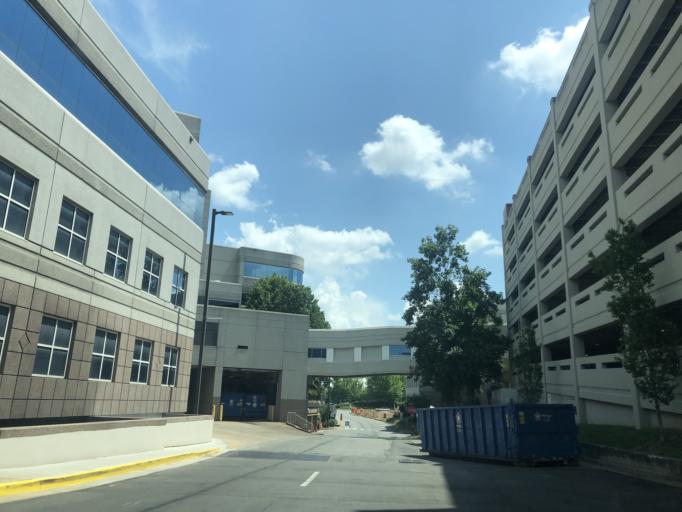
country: US
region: Tennessee
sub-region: Davidson County
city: Nashville
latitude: 36.1537
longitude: -86.8098
